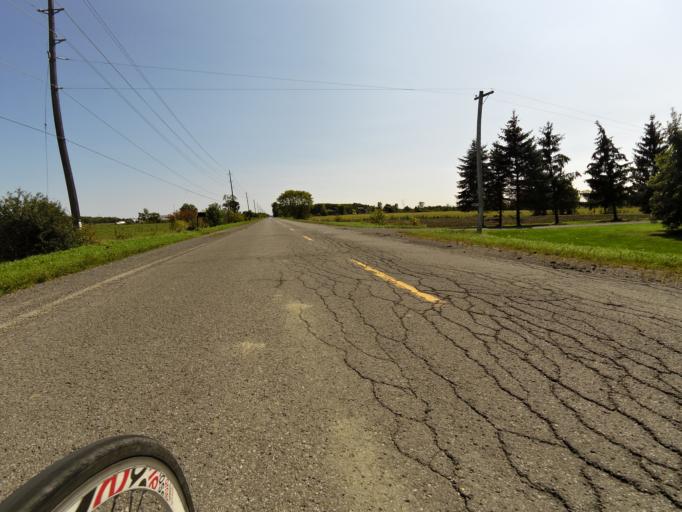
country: CA
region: Ontario
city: Arnprior
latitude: 45.4809
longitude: -76.1233
